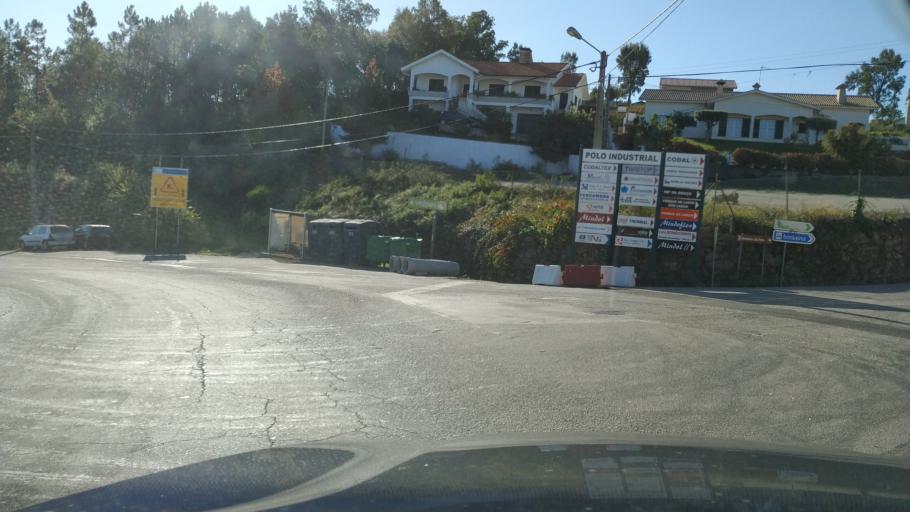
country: PT
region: Aveiro
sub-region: Vale de Cambra
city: Vale de Cambra
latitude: 40.8726
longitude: -8.4145
